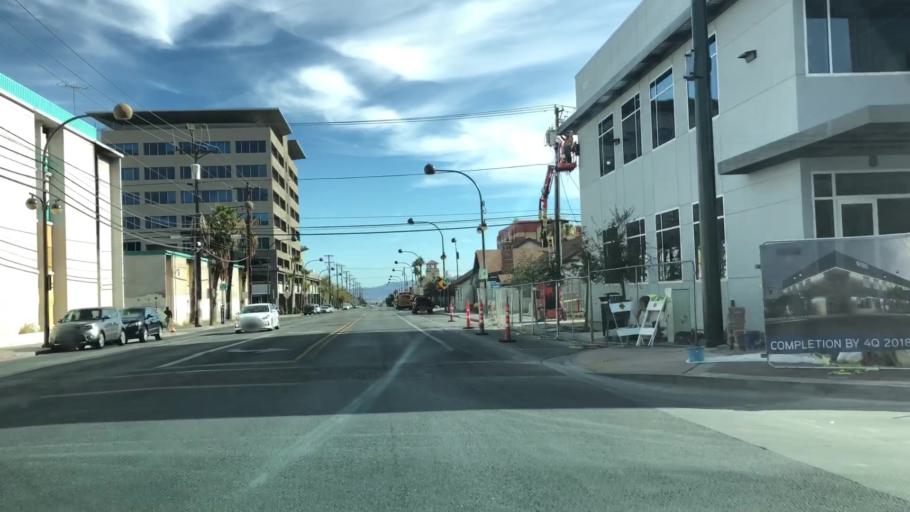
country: US
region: Nevada
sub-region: Clark County
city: Las Vegas
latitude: 36.1664
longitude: -115.1411
